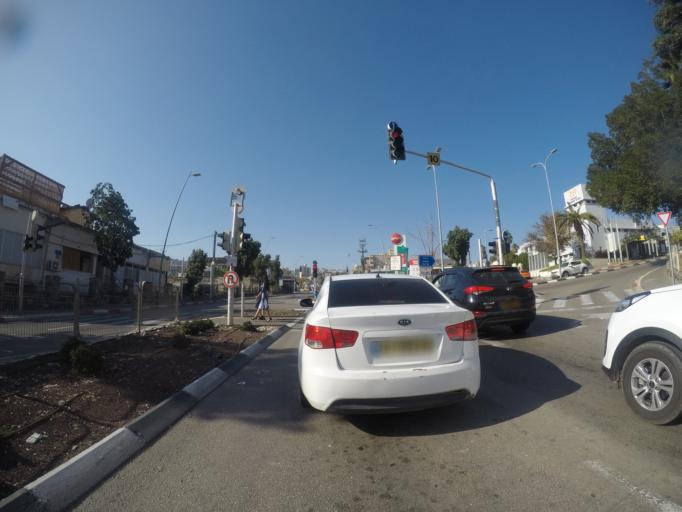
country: IL
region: Northern District
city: Tiberias
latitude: 32.7914
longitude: 35.5370
